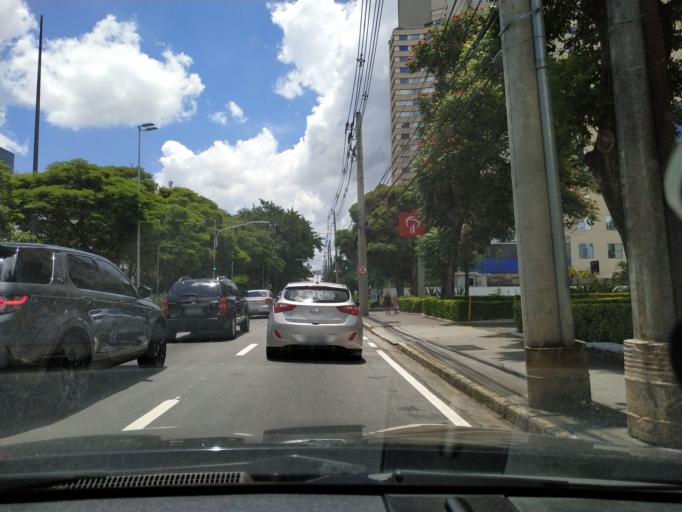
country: BR
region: Sao Paulo
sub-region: Carapicuiba
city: Carapicuiba
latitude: -23.4979
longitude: -46.8482
